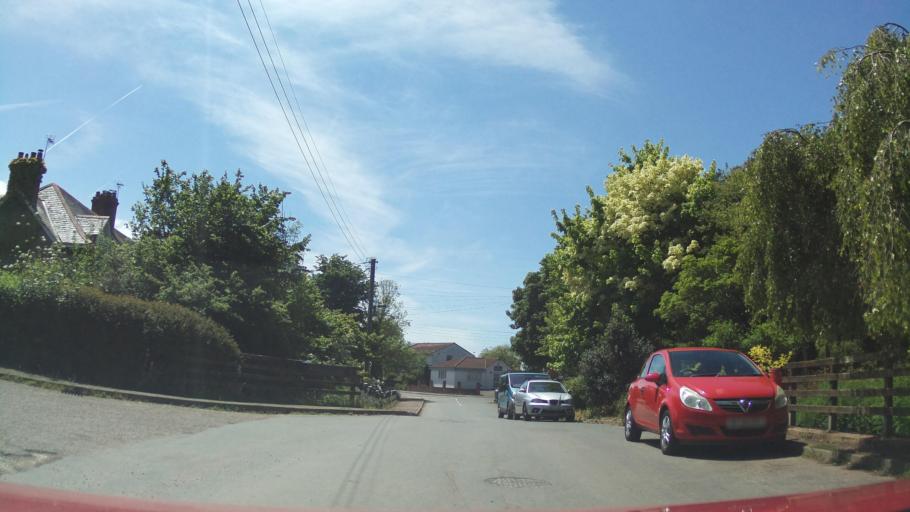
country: GB
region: England
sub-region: Devon
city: Exmouth
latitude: 50.6231
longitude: -3.3730
